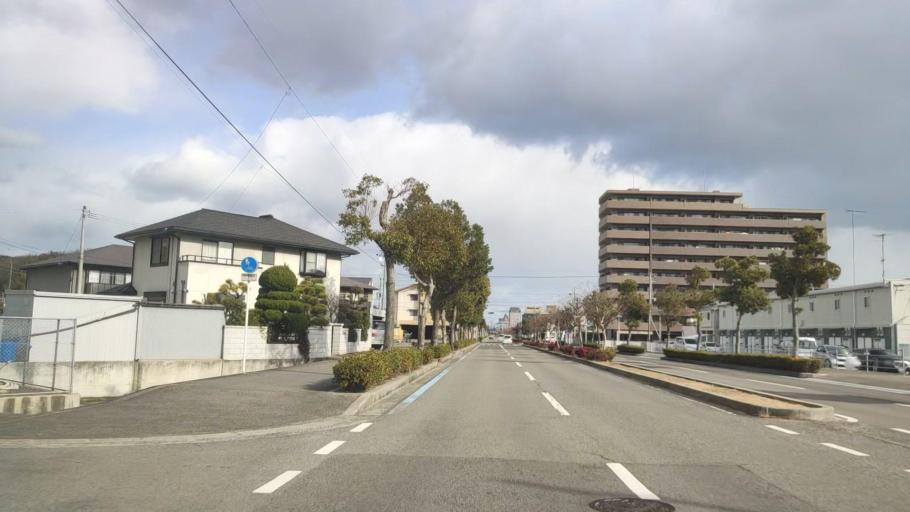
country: JP
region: Ehime
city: Hojo
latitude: 34.0604
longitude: 132.9840
